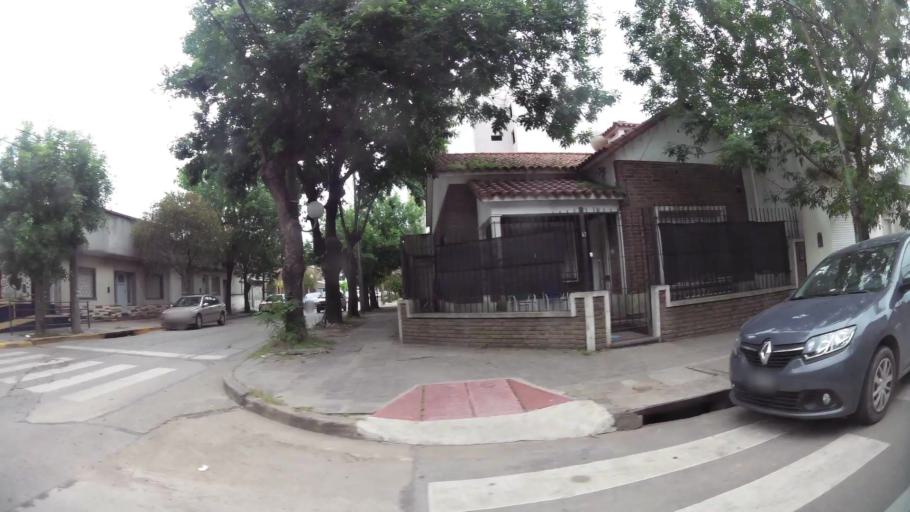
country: AR
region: Buenos Aires
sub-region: Partido de Zarate
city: Zarate
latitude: -34.0938
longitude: -59.0277
